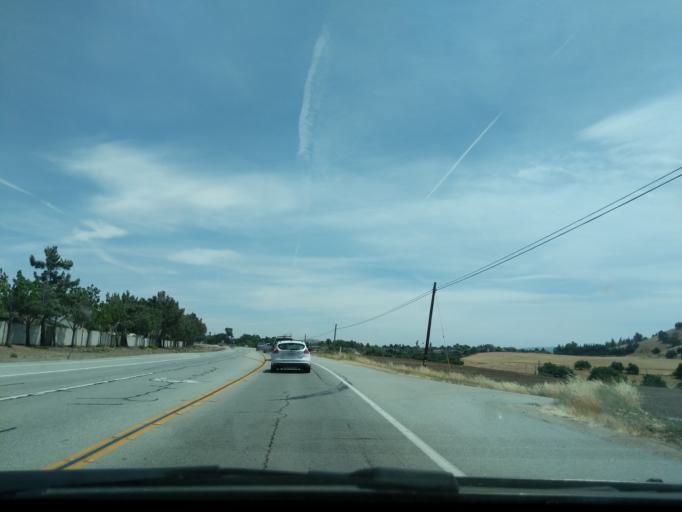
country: US
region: California
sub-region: San Benito County
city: Ridgemark
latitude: 36.8260
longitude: -121.3818
